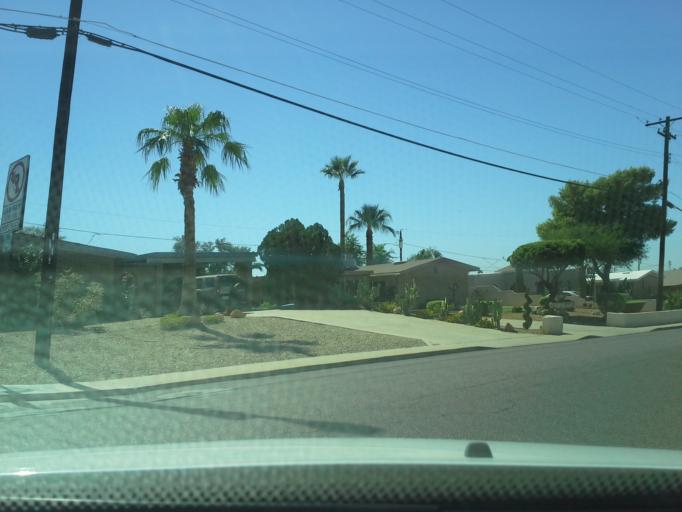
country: US
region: Arizona
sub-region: Maricopa County
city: Paradise Valley
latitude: 33.5678
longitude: -112.0526
